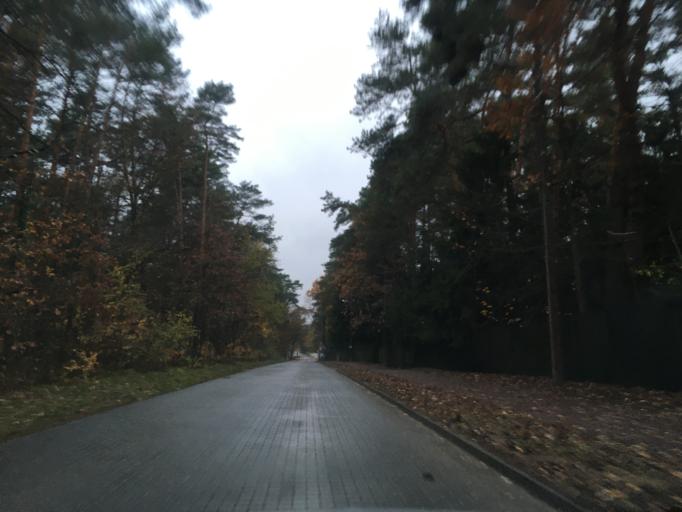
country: PL
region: Masovian Voivodeship
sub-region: Powiat piaseczynski
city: Lesznowola
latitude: 52.0895
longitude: 20.8987
